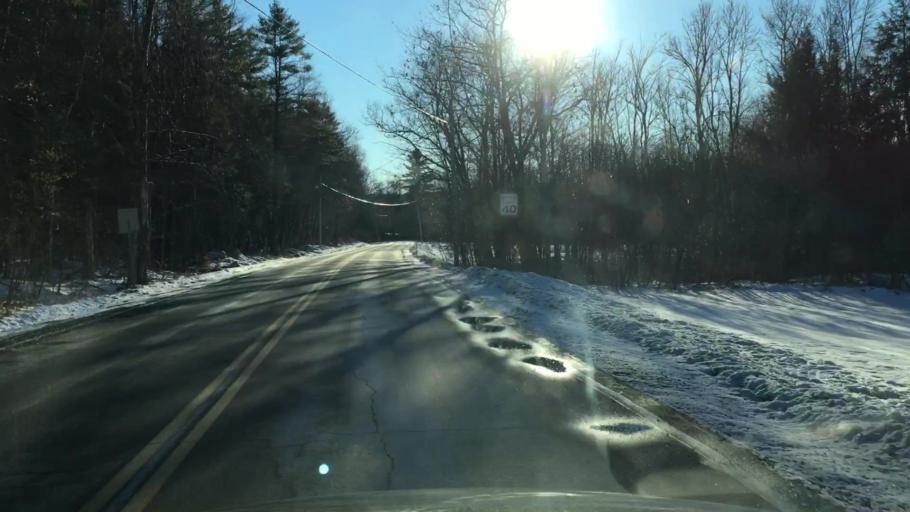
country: US
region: New Hampshire
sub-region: Grafton County
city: Woodsville
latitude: 44.2016
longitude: -72.0556
